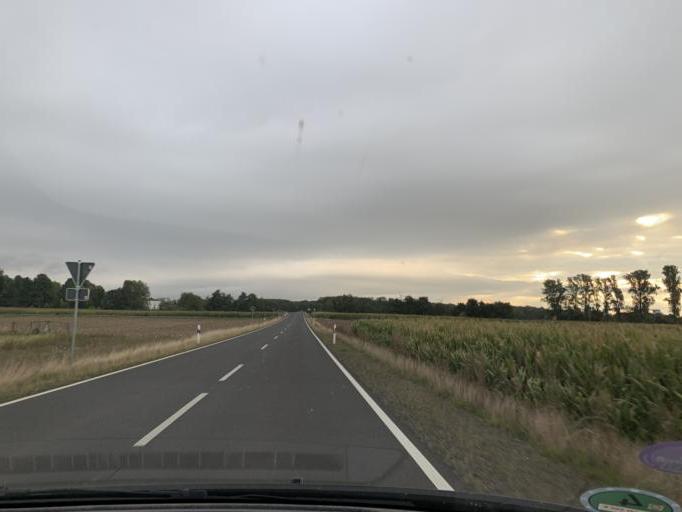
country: DE
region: North Rhine-Westphalia
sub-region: Regierungsbezirk Koln
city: Niederzier
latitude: 50.8405
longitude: 6.4297
